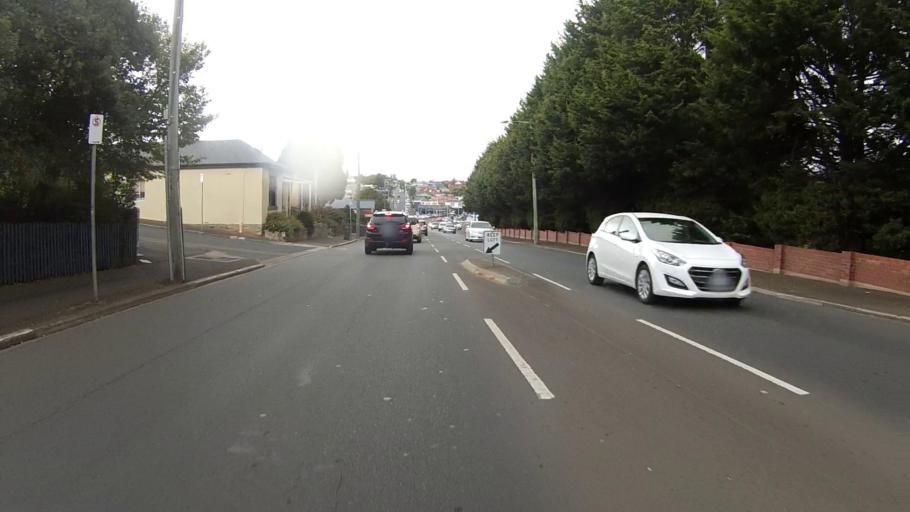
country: AU
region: Tasmania
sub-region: Hobart
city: New Town
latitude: -42.8544
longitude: 147.3018
